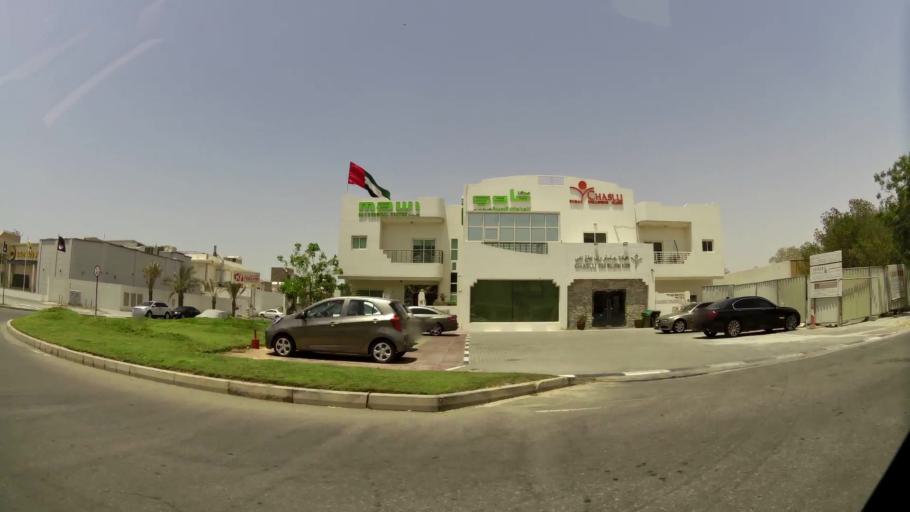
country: AE
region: Dubai
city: Dubai
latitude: 25.1716
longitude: 55.2186
